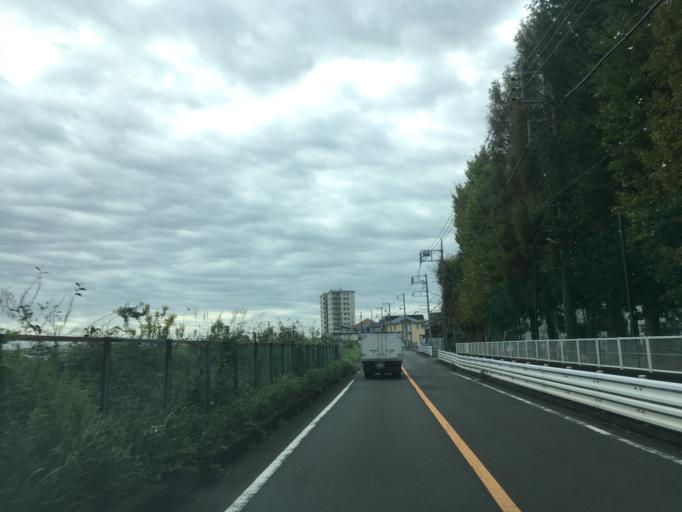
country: JP
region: Tokyo
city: Chofugaoka
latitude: 35.6447
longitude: 139.5210
